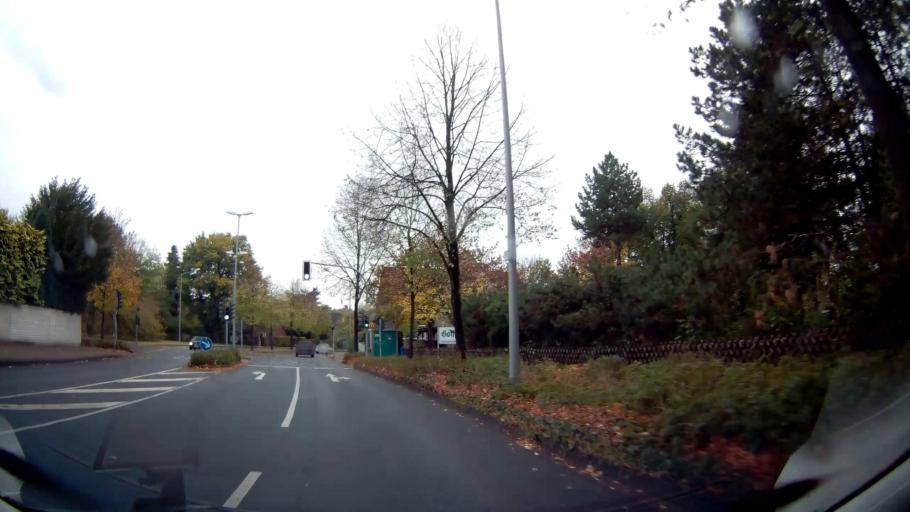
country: DE
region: North Rhine-Westphalia
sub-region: Regierungsbezirk Munster
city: Gladbeck
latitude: 51.5700
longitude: 6.9728
